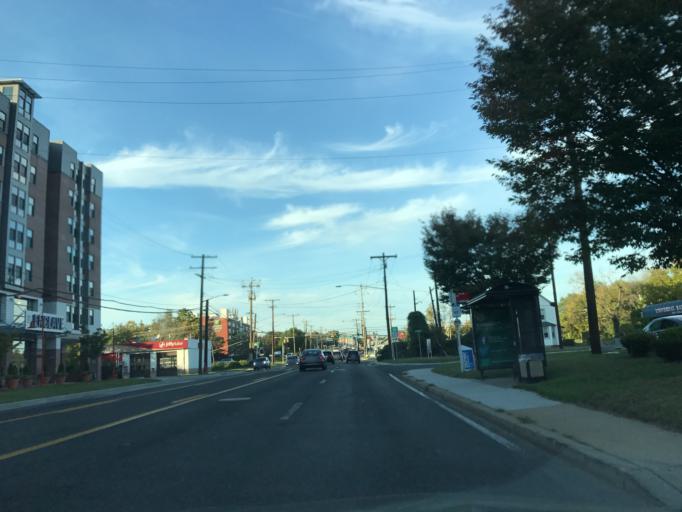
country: US
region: Maryland
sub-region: Prince George's County
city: College Park
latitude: 38.9971
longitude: -76.9316
